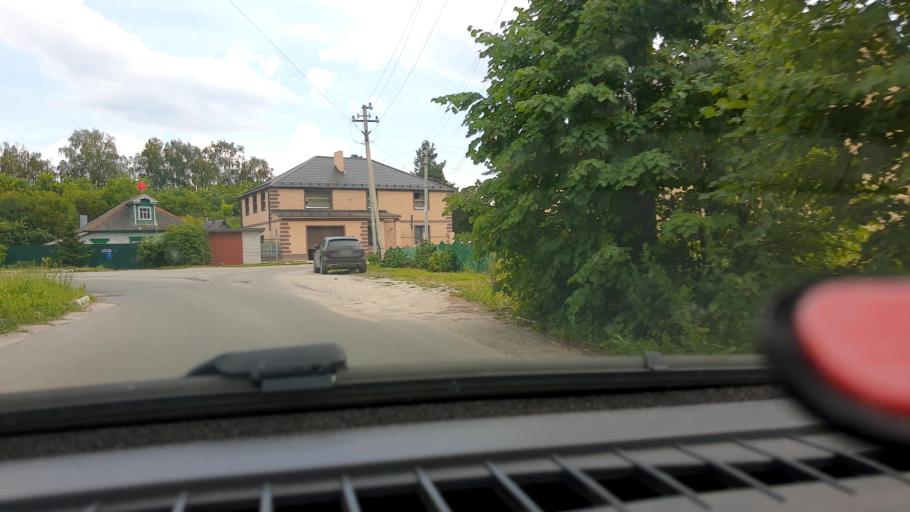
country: RU
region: Nizjnij Novgorod
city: Gorodets
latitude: 56.6351
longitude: 43.4753
